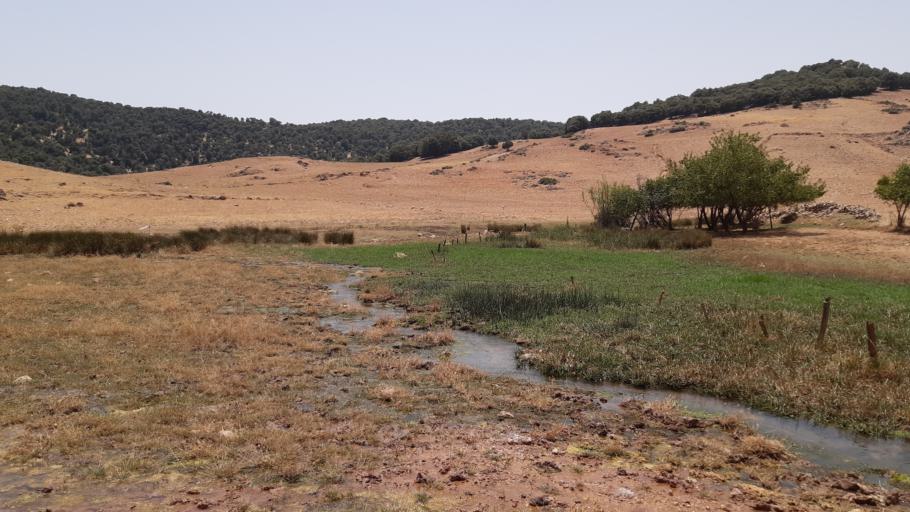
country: MA
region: Meknes-Tafilalet
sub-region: Khenifra
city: Khenifra
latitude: 33.0254
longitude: -5.5018
